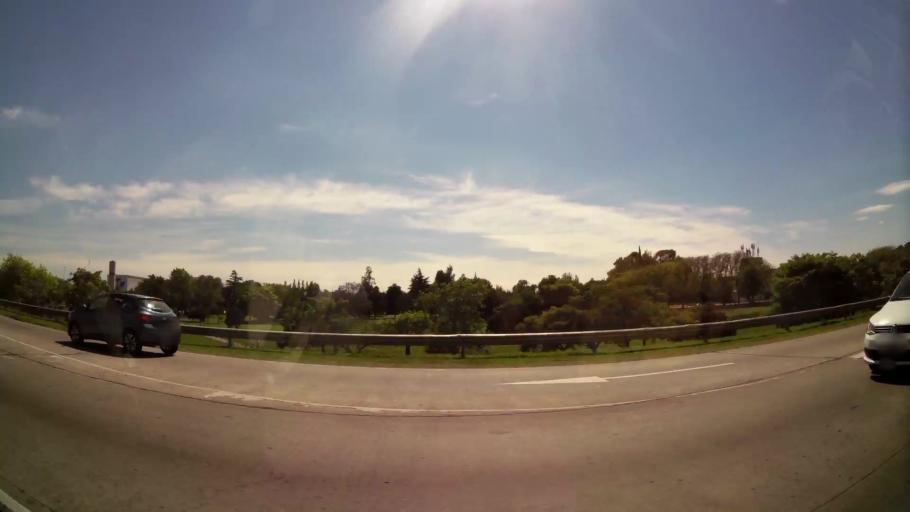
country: AR
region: Buenos Aires
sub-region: Partido de Tigre
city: Tigre
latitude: -34.4725
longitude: -58.5661
